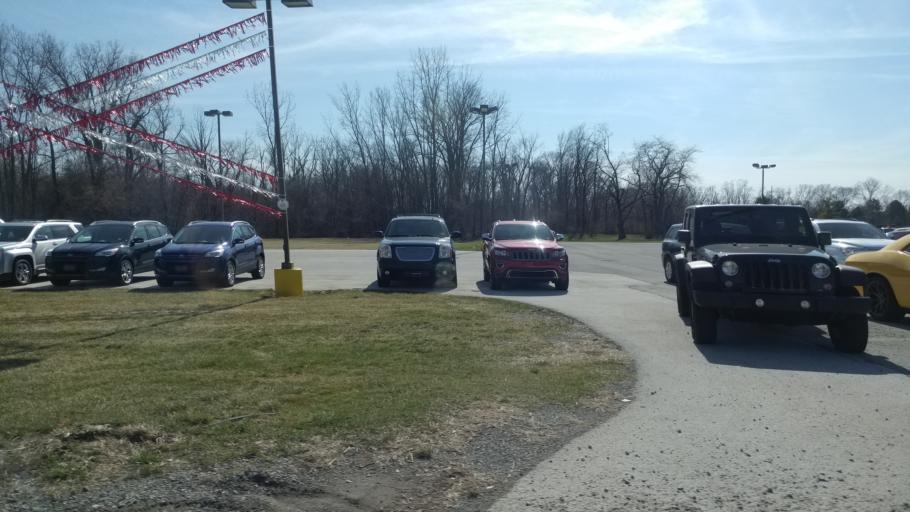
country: US
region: Ohio
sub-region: Hancock County
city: Findlay
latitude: 41.0591
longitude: -83.6794
